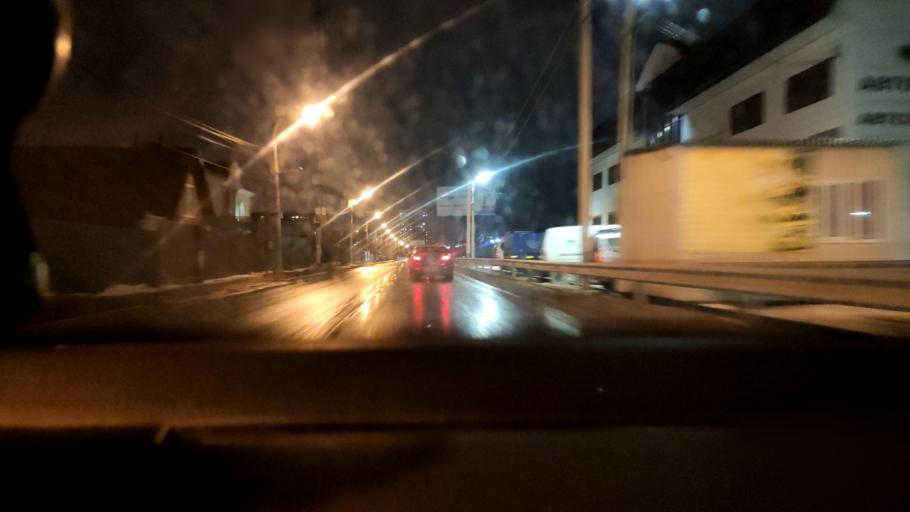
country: RU
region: Moskovskaya
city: Zhukovskiy
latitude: 55.5899
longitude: 38.1018
